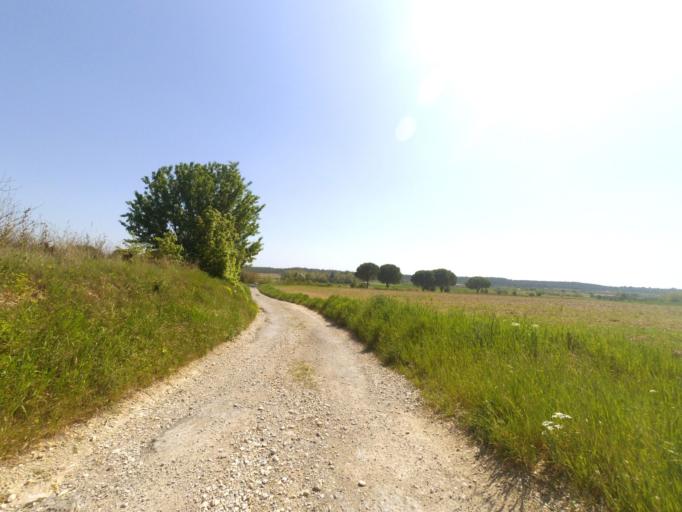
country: FR
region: Languedoc-Roussillon
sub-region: Departement du Gard
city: Calvisson
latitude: 43.7775
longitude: 4.1824
